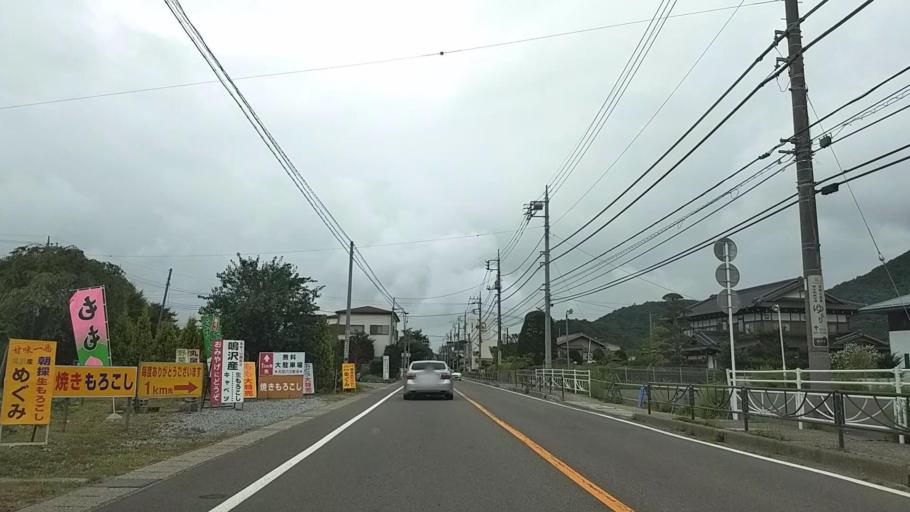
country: JP
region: Yamanashi
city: Fujikawaguchiko
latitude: 35.4809
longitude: 138.7059
